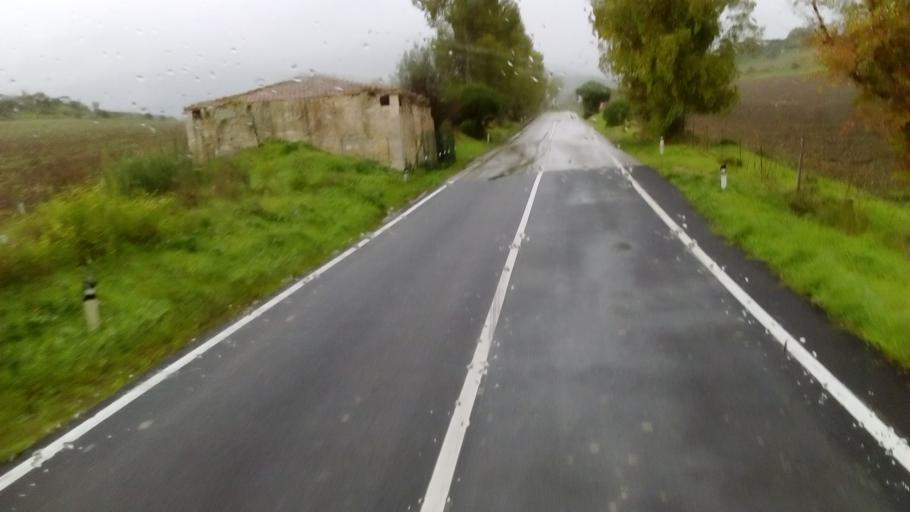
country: IT
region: Sicily
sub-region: Enna
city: Pietraperzia
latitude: 37.4607
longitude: 14.1772
